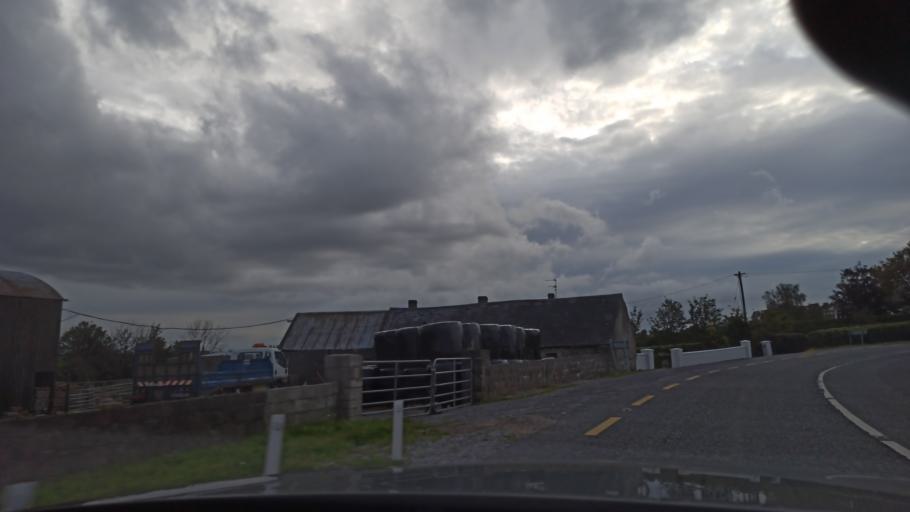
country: IE
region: Munster
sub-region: South Tipperary
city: Cluain Meala
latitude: 52.3826
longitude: -7.7248
